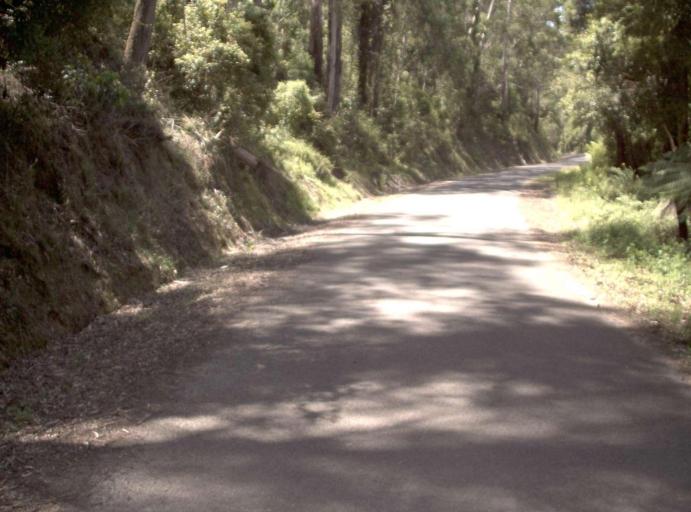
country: AU
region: New South Wales
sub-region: Bombala
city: Bombala
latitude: -37.4533
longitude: 148.9311
